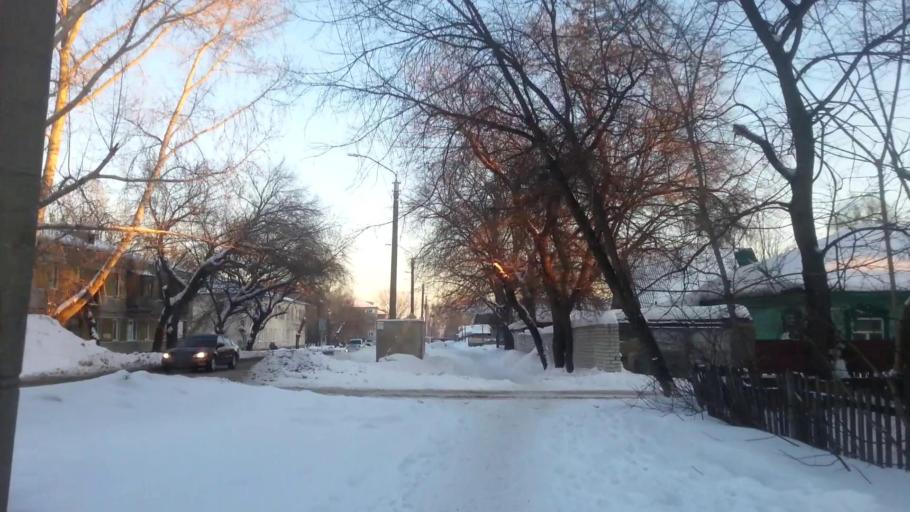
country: RU
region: Altai Krai
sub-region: Gorod Barnaulskiy
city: Barnaul
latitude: 53.3567
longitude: 83.7009
